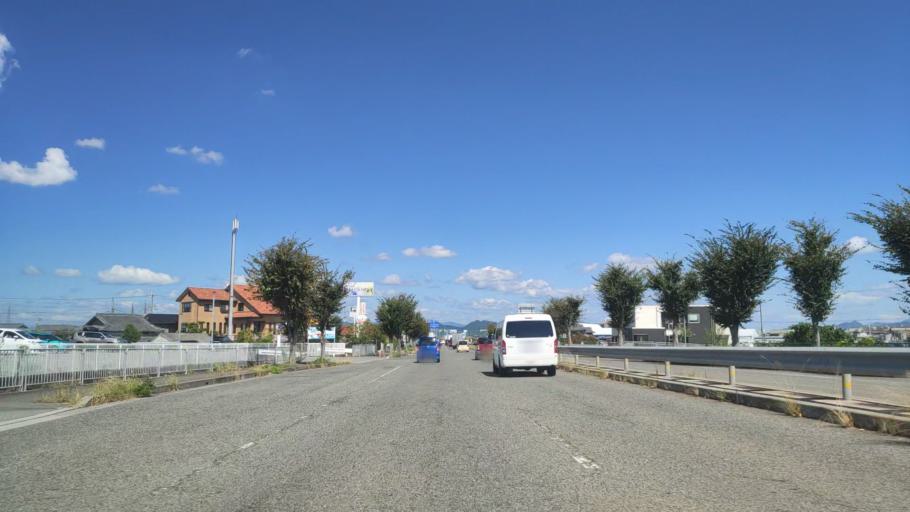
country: JP
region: Hyogo
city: Ono
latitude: 34.8813
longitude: 134.9504
